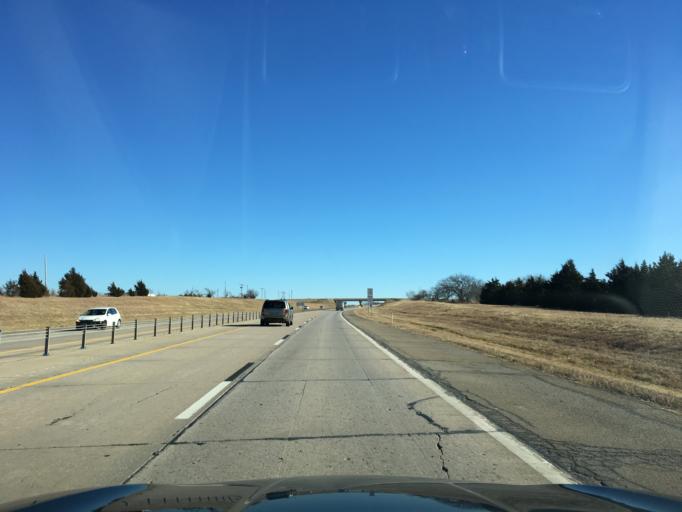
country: US
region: Oklahoma
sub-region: Pawnee County
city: Pawnee
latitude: 36.2390
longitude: -96.9320
